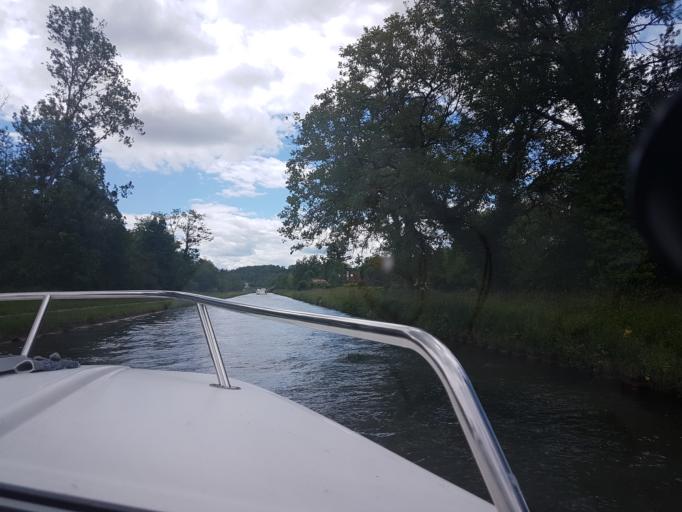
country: FR
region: Bourgogne
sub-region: Departement de l'Yonne
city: Vermenton
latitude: 47.6073
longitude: 3.6840
